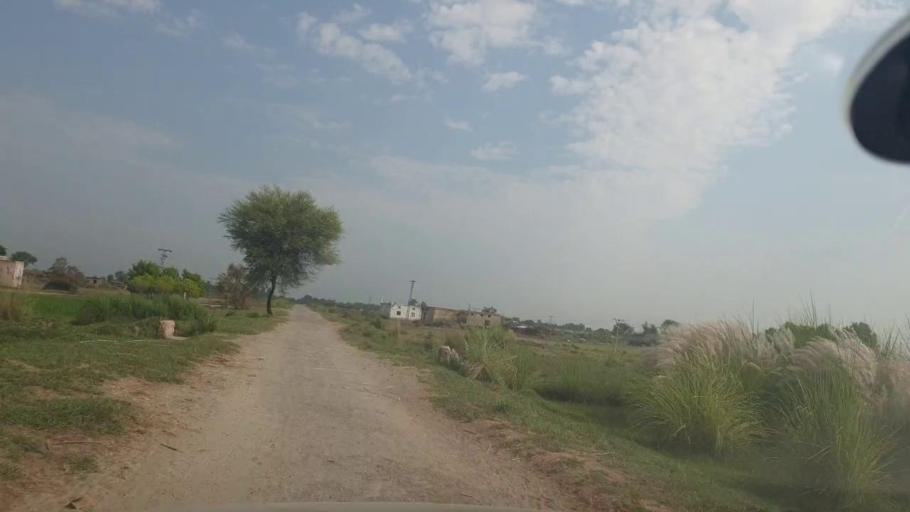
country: PK
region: Balochistan
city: Mehrabpur
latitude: 28.0540
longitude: 68.1236
